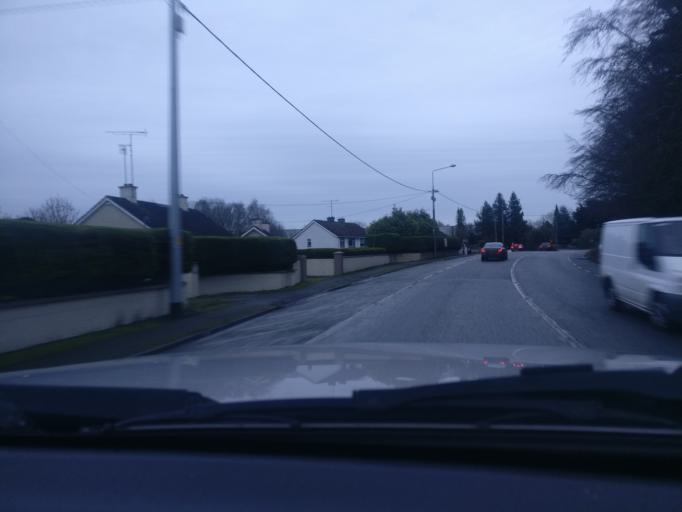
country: IE
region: Leinster
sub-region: An Mhi
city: Navan
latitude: 53.6561
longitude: -6.7052
